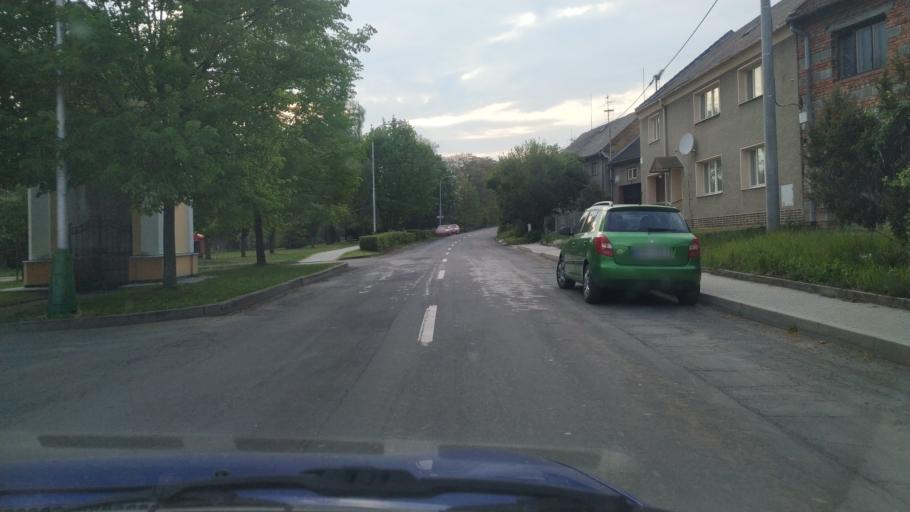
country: CZ
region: Olomoucky
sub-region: Okres Olomouc
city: Slatinice
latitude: 49.5511
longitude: 17.1106
